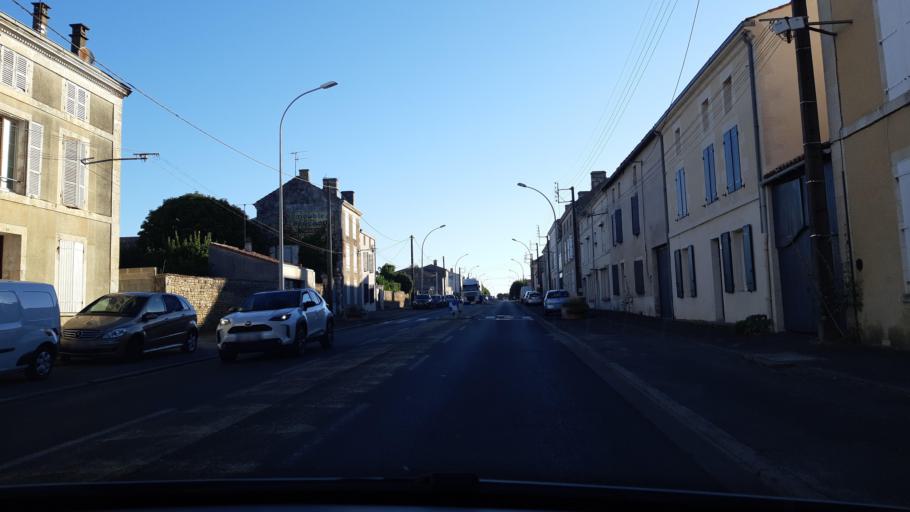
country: FR
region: Poitou-Charentes
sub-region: Departement des Deux-Sevres
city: La Creche
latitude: 46.3634
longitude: -0.2973
